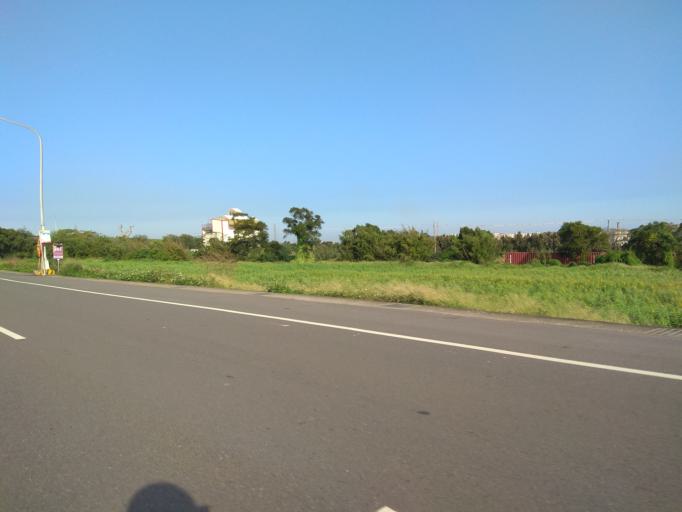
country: TW
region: Taiwan
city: Taoyuan City
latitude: 24.9697
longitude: 121.1363
